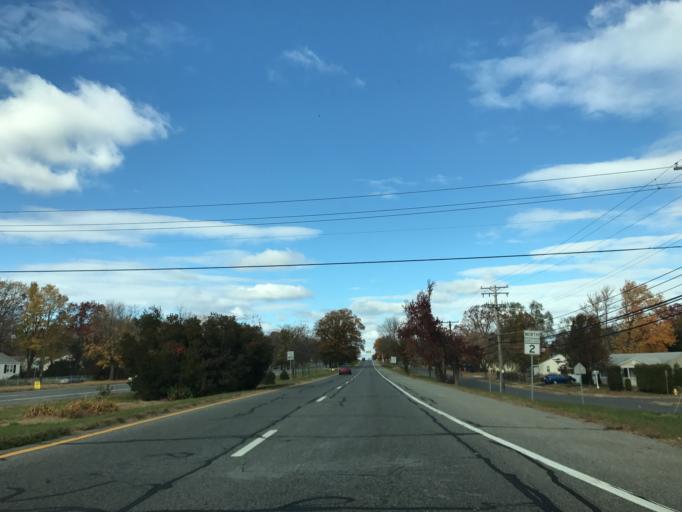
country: US
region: Maryland
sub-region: Anne Arundel County
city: Glen Burnie
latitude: 39.1538
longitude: -76.6146
